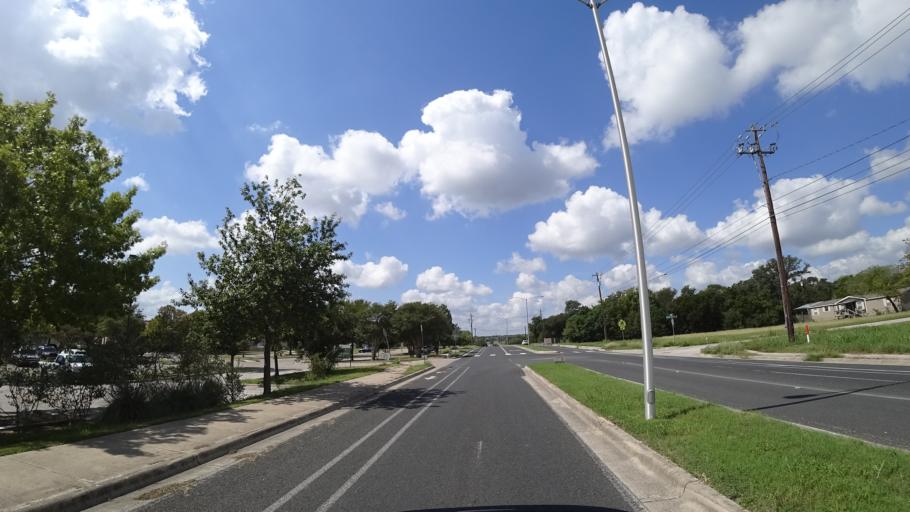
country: US
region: Texas
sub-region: Travis County
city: Onion Creek
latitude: 30.1857
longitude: -97.8012
